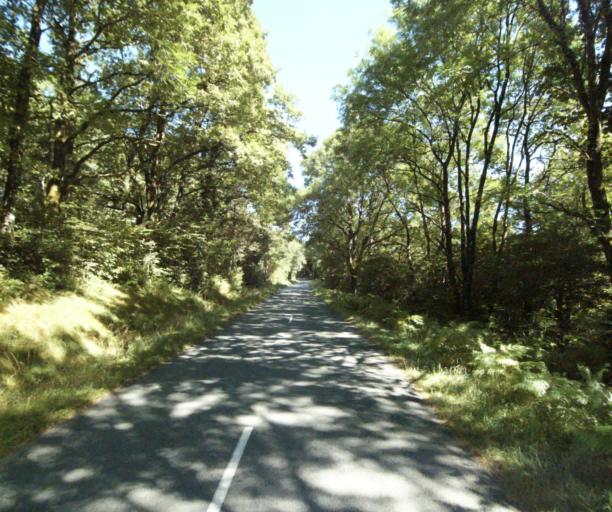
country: FR
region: Midi-Pyrenees
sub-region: Departement du Tarn
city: Soreze
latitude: 43.4331
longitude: 2.1136
